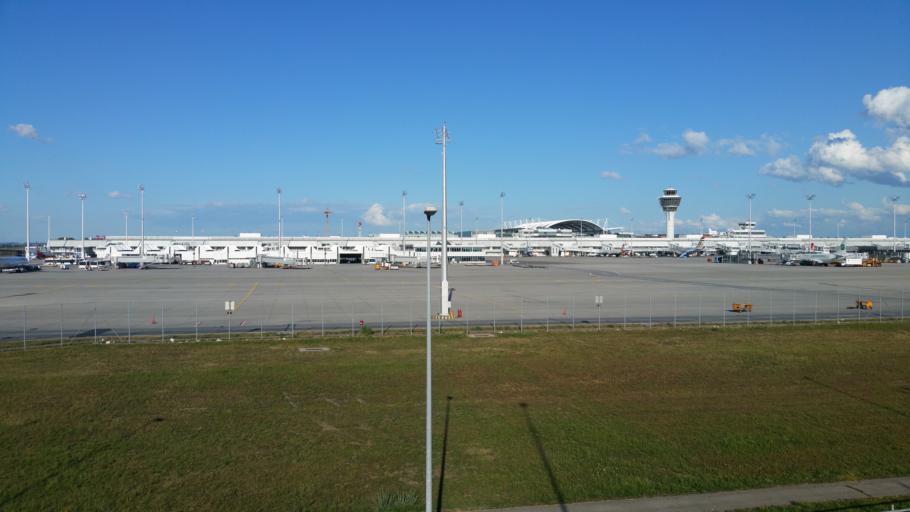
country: DE
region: Bavaria
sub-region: Upper Bavaria
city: Hallbergmoos
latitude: 48.3561
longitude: 11.7747
